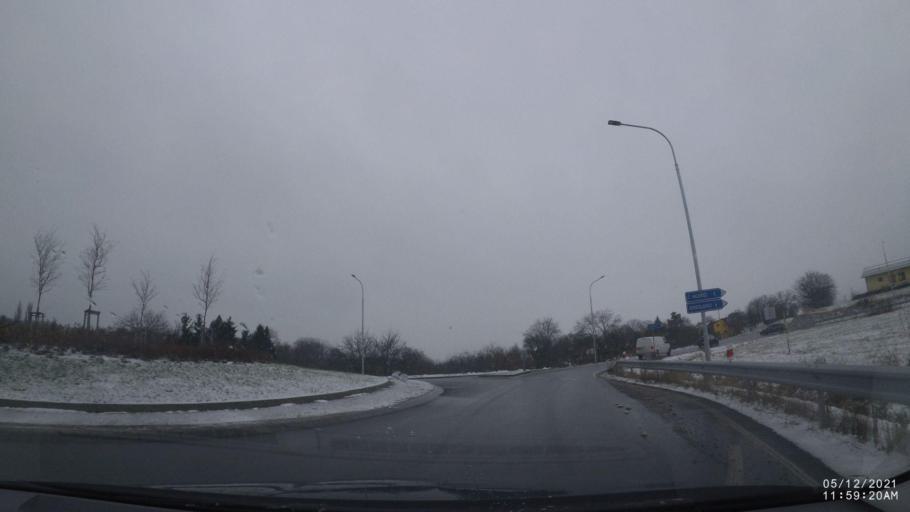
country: CZ
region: Kralovehradecky
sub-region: Okres Rychnov nad Kneznou
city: Opocno
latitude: 50.2733
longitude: 16.1012
